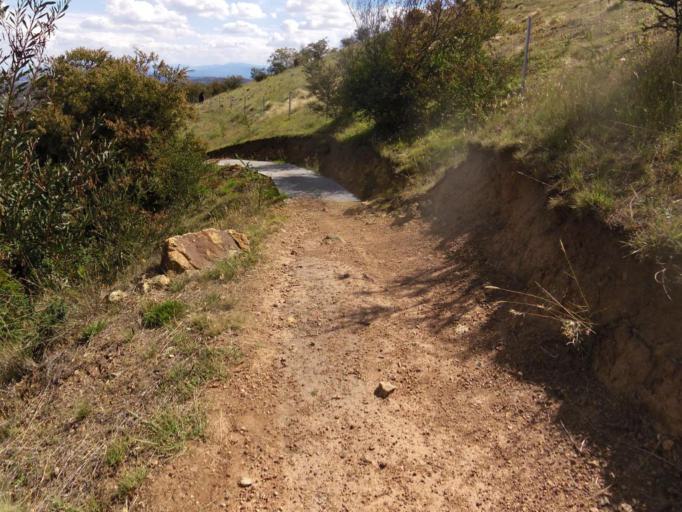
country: AU
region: Australian Capital Territory
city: Belconnen
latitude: -35.1490
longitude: 149.0891
